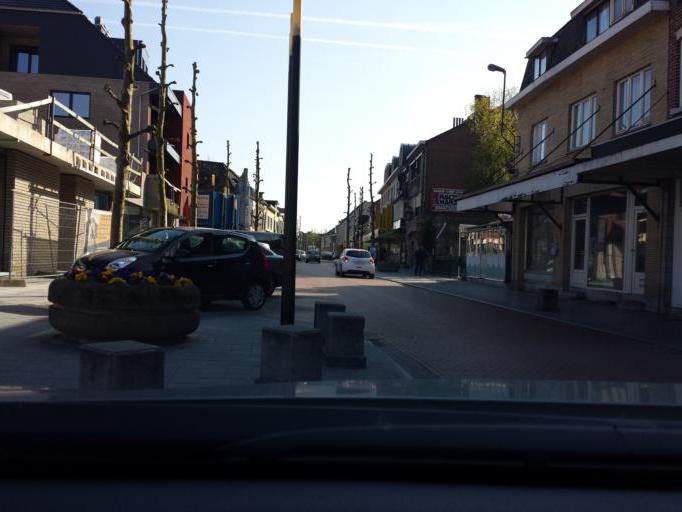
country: BE
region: Flanders
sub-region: Provincie Limburg
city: Maasmechelen
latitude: 50.9871
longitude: 5.6941
